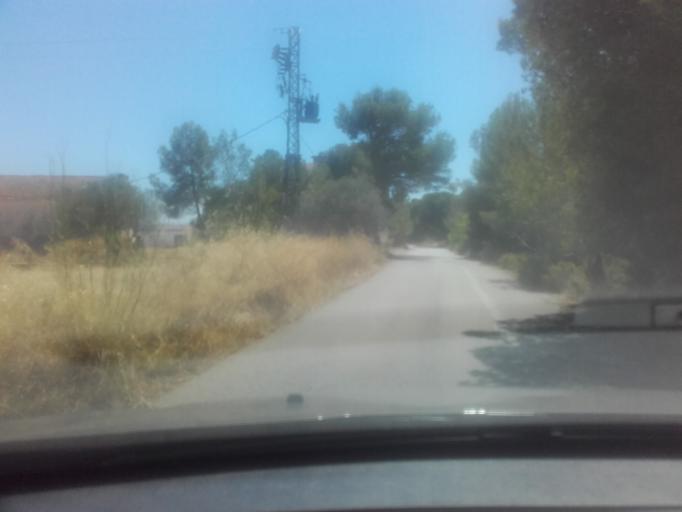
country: ES
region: Catalonia
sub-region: Provincia de Tarragona
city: Santa Oliva
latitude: 41.2577
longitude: 1.5284
